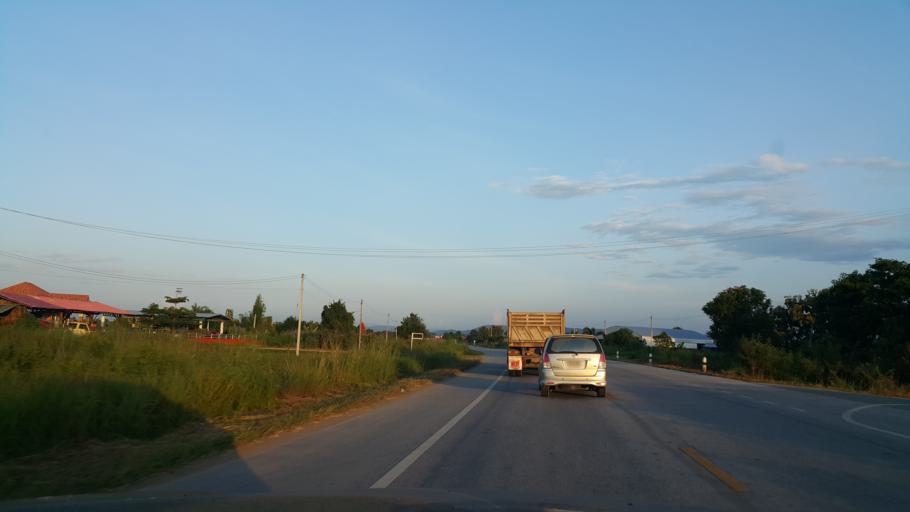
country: TH
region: Lamphun
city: Pa Sang
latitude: 18.4912
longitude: 98.8991
